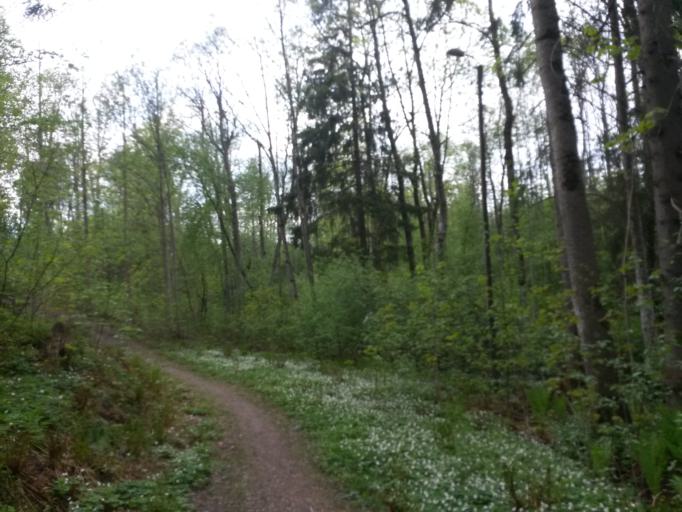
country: NO
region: Akershus
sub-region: Asker
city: Asker
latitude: 59.8375
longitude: 10.4107
